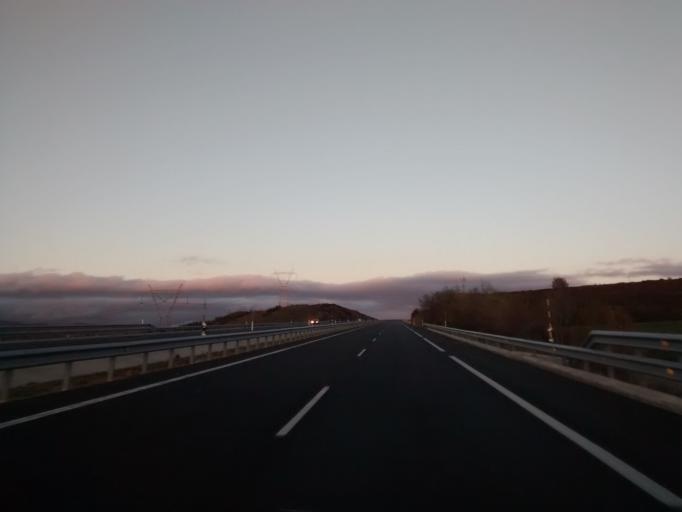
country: ES
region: Castille and Leon
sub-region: Provincia de Palencia
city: Aguilar de Campoo
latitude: 42.8018
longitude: -4.2334
